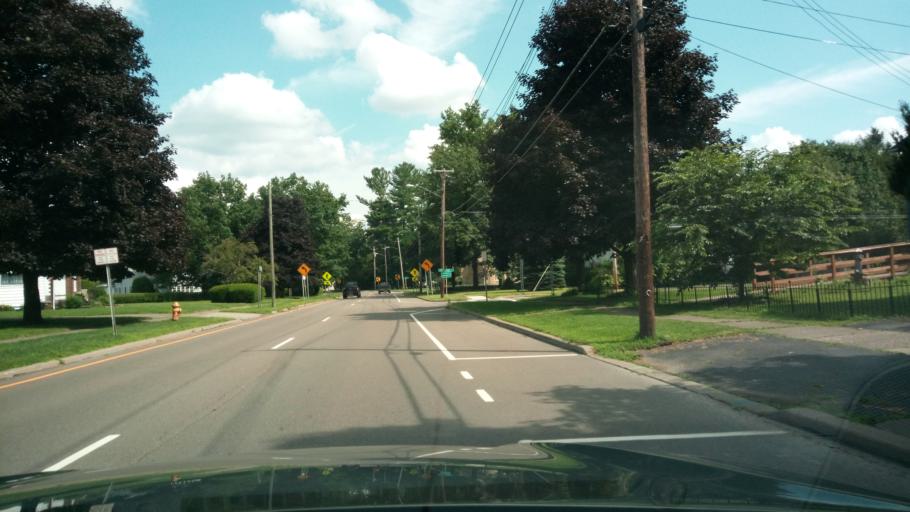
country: US
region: New York
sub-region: Chemung County
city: West Elmira
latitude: 42.0786
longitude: -76.8537
